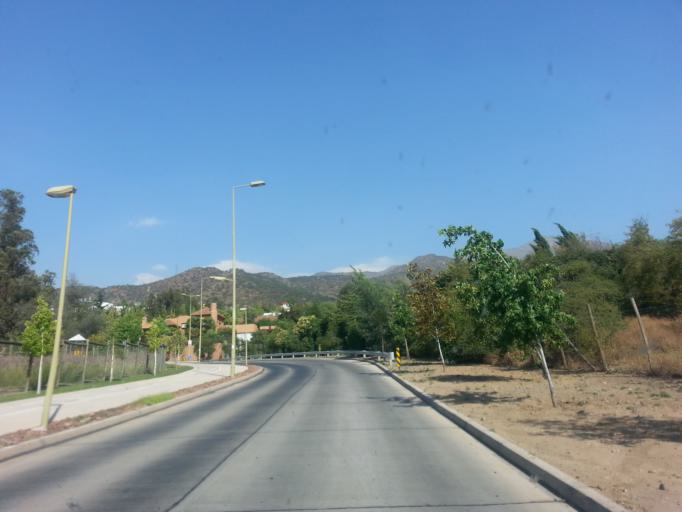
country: CL
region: Santiago Metropolitan
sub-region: Provincia de Santiago
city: Villa Presidente Frei, Nunoa, Santiago, Chile
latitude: -33.3784
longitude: -70.5028
